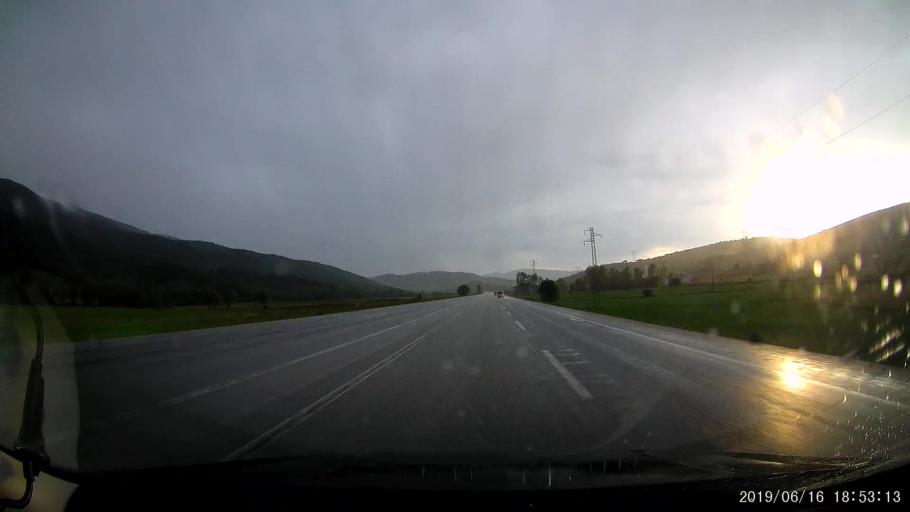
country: TR
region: Erzincan
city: Catalcam
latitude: 39.8994
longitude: 38.8827
